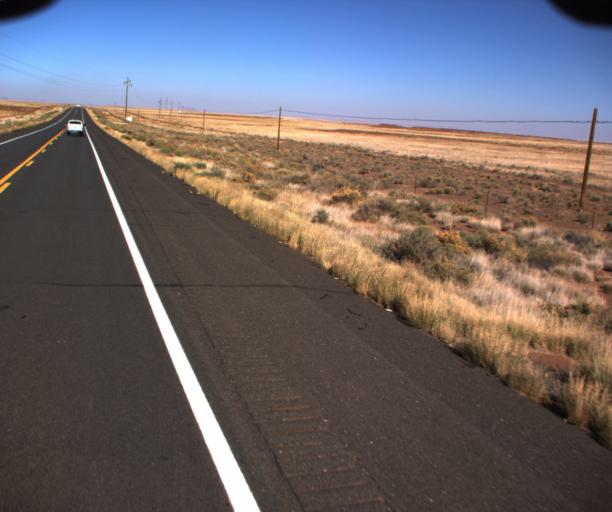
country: US
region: Arizona
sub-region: Coconino County
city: Flagstaff
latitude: 35.6598
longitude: -111.5133
